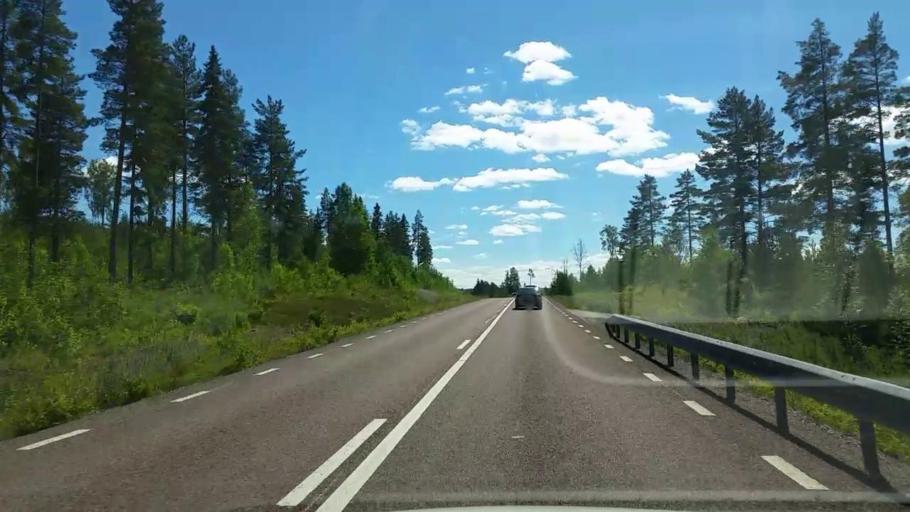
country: SE
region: Gaevleborg
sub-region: Ovanakers Kommun
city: Edsbyn
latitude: 61.2415
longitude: 15.8825
